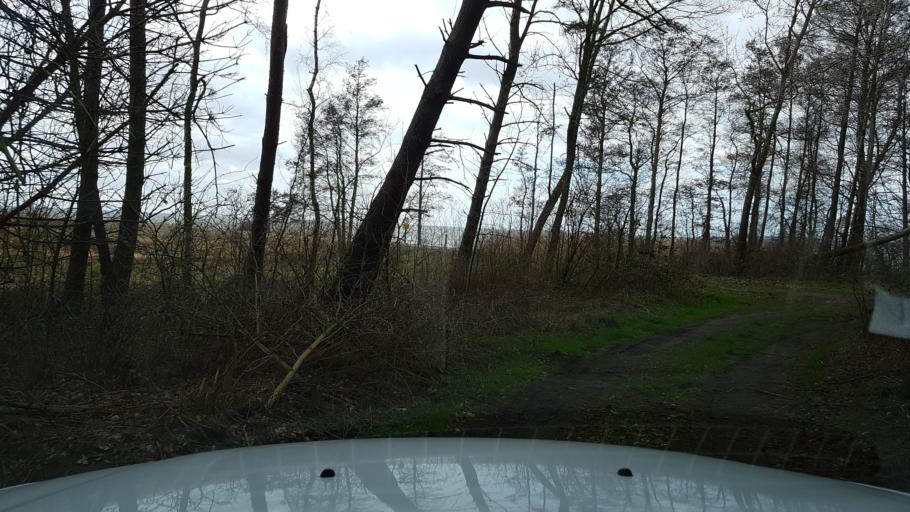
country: PL
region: West Pomeranian Voivodeship
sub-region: Powiat kamienski
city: Wolin
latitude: 53.7893
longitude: 14.6143
